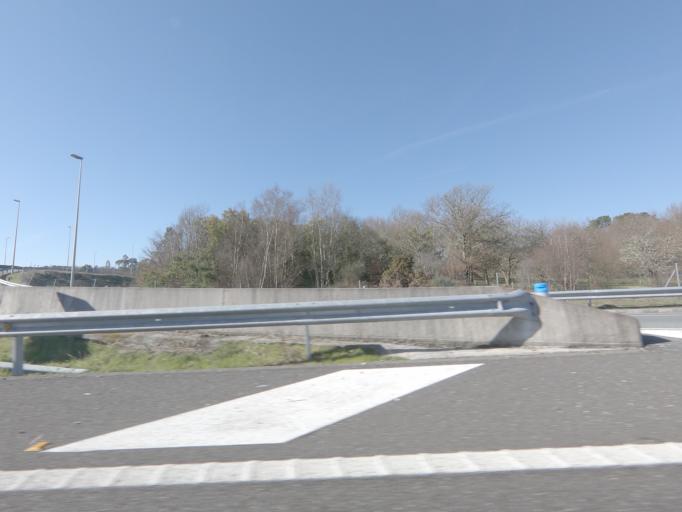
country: ES
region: Galicia
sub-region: Provincia de Ourense
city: Maside
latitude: 42.4081
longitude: -8.0117
